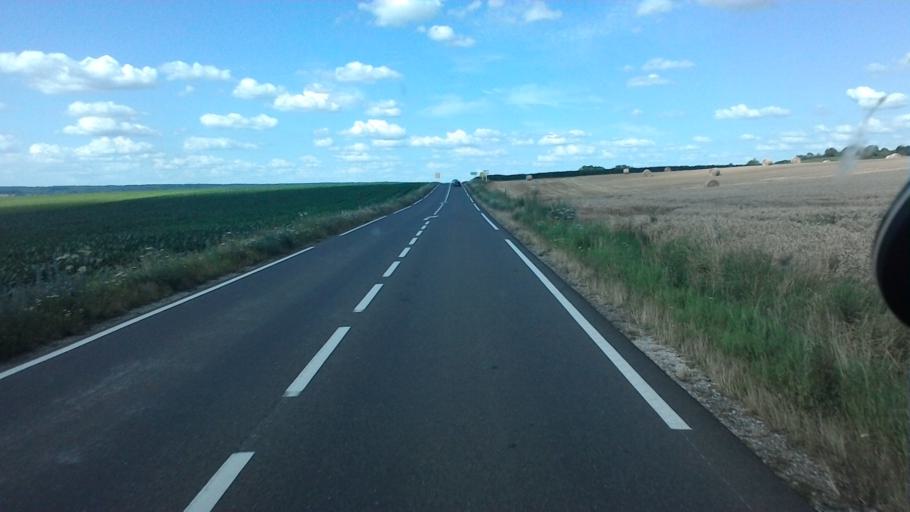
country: FR
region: Franche-Comte
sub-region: Departement de la Haute-Saone
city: Gy
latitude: 47.3965
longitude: 5.7941
